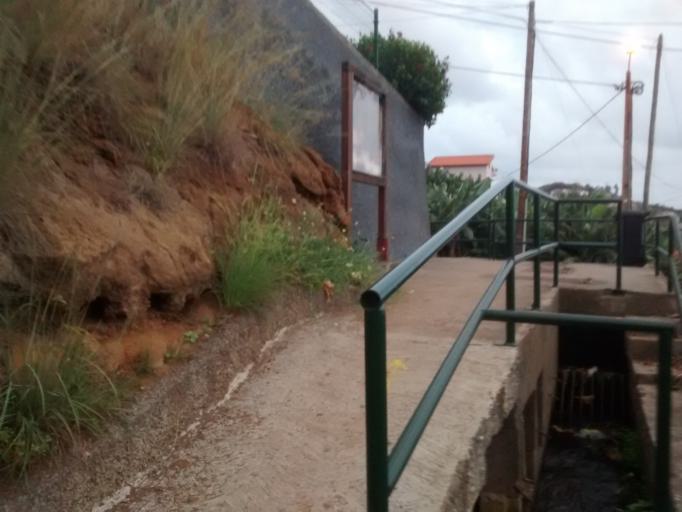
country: PT
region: Madeira
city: Camara de Lobos
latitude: 32.6540
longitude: -16.9623
